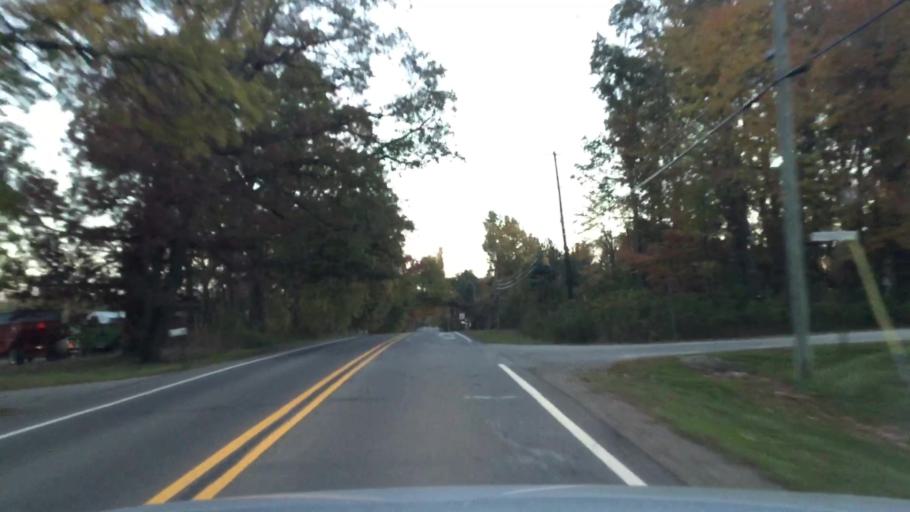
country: US
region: Michigan
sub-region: Lapeer County
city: Almont
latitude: 42.8711
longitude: -83.1431
